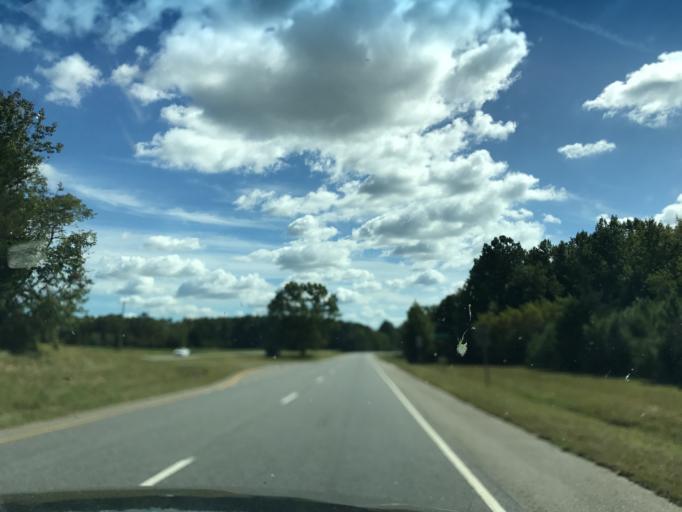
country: US
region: Virginia
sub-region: King and Queen County
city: King and Queen Court House
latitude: 37.7529
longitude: -76.7218
